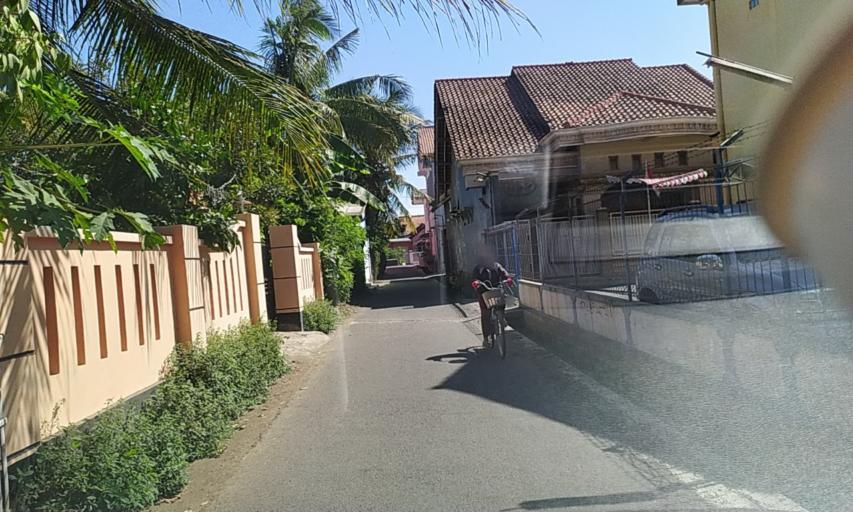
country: ID
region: Central Java
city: Rejanegara
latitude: -7.6882
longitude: 109.0351
